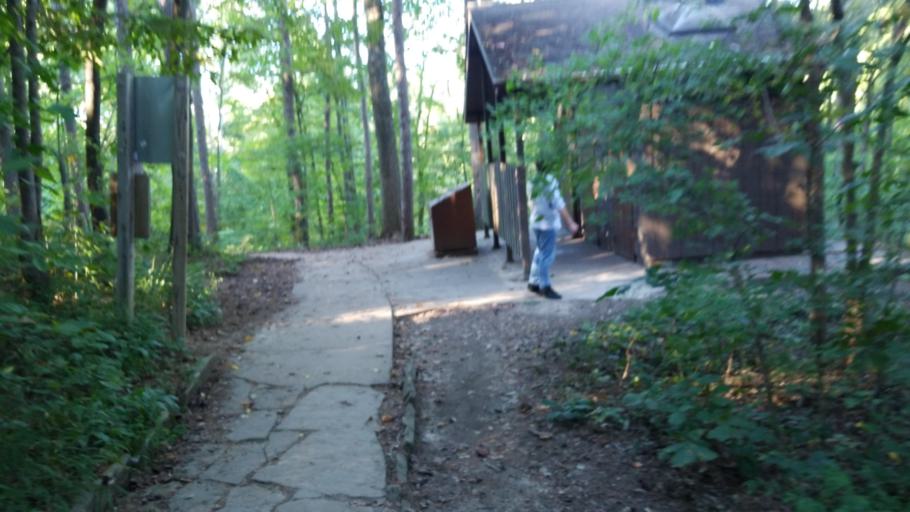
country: US
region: Illinois
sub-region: Hardin County
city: Elizabethtown
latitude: 37.6041
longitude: -88.3845
